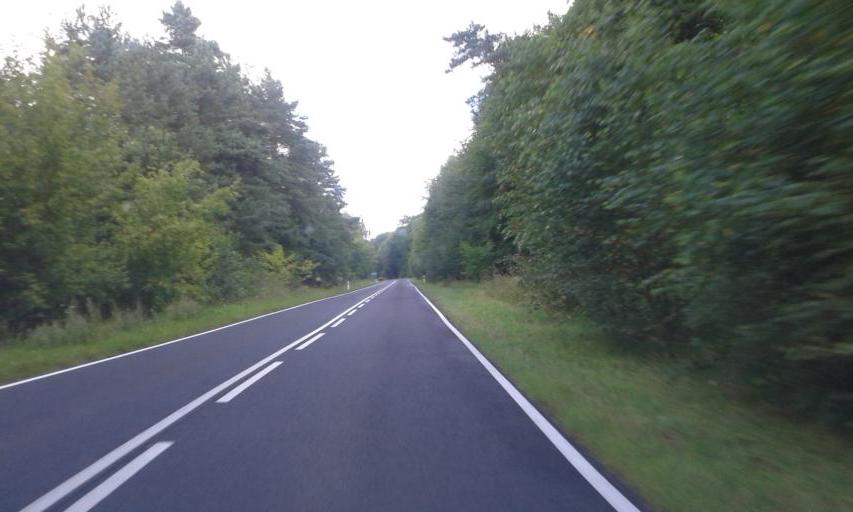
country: PL
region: West Pomeranian Voivodeship
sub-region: Powiat koszalinski
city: Polanow
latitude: 54.0129
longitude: 16.7194
